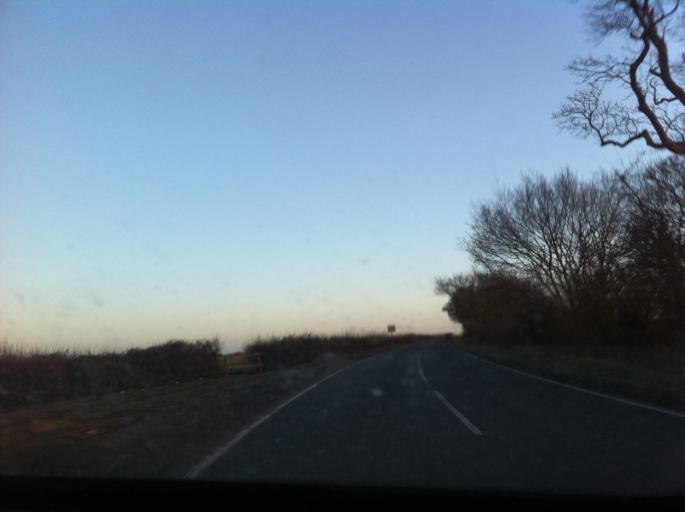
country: GB
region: England
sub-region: Northamptonshire
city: Irchester
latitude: 52.2689
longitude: -0.6544
